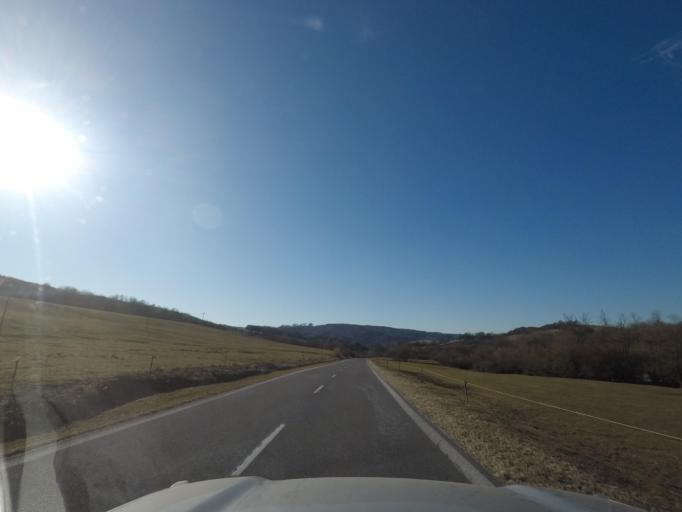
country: PL
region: Subcarpathian Voivodeship
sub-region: Powiat sanocki
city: Komancza
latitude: 49.1592
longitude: 22.0521
